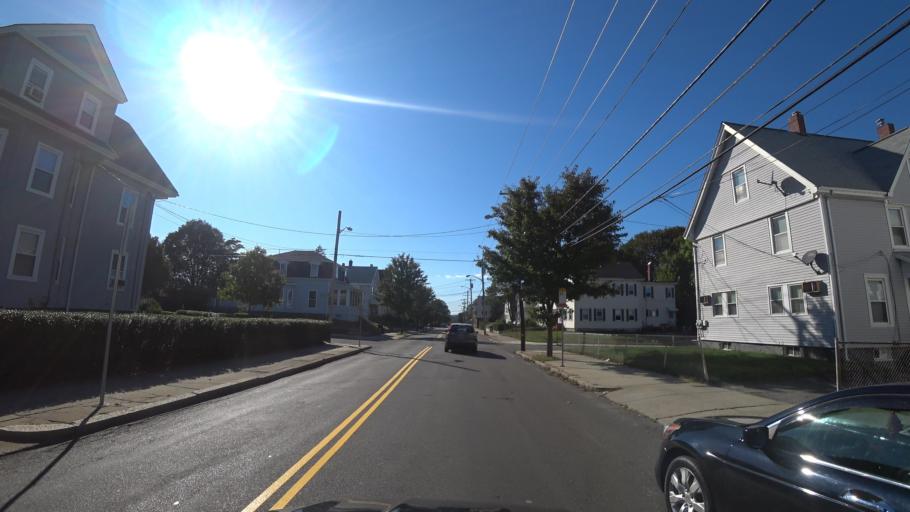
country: US
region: Massachusetts
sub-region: Middlesex County
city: Malden
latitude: 42.4183
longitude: -71.0676
